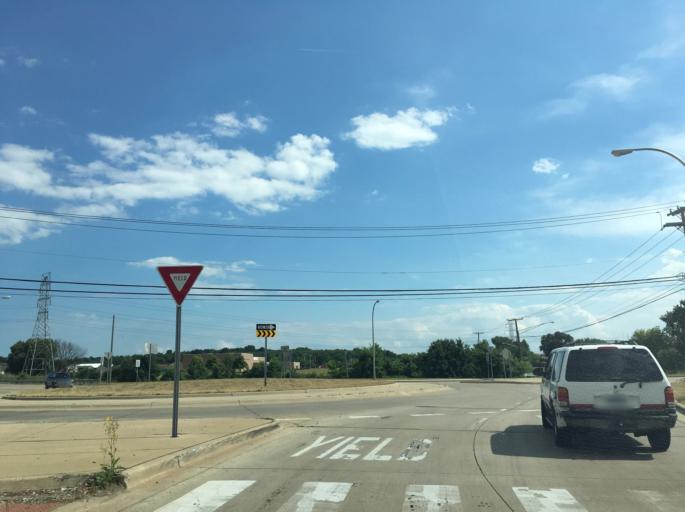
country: US
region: Michigan
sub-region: Macomb County
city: Clinton
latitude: 42.6118
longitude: -82.9324
